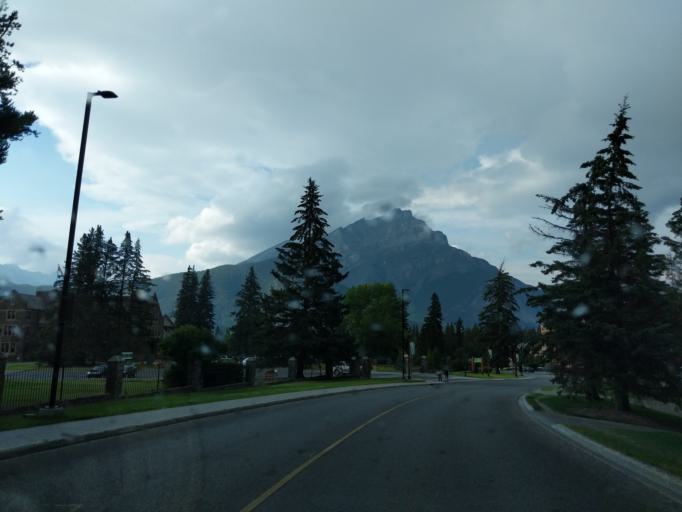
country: CA
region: Alberta
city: Banff
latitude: 51.1699
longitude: -115.5705
